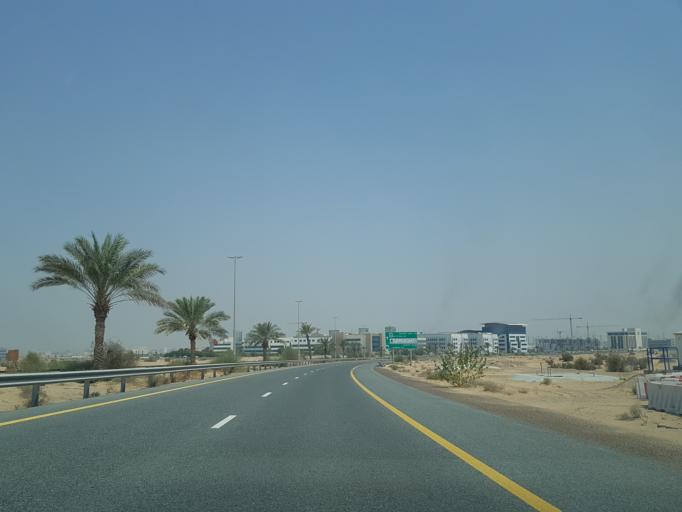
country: AE
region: Ash Shariqah
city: Sharjah
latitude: 25.1193
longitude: 55.4277
